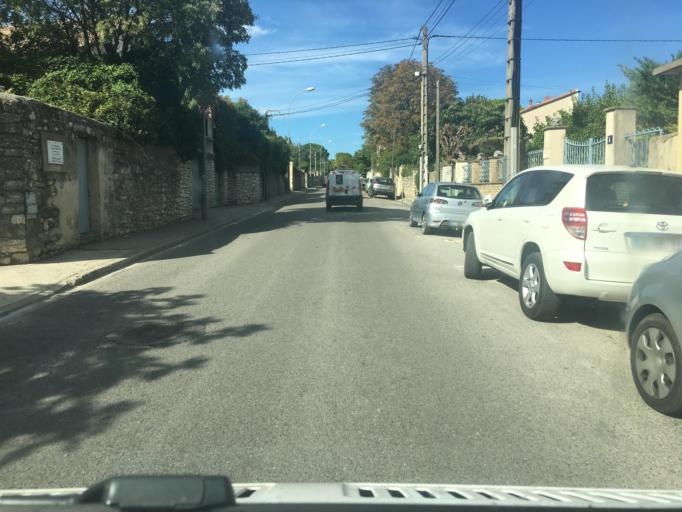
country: FR
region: Languedoc-Roussillon
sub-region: Departement du Gard
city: Uzes
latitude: 44.0162
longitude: 4.4169
